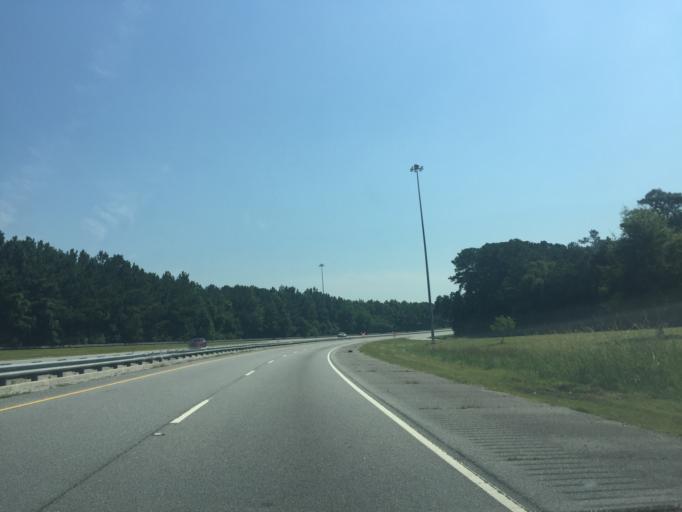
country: US
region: Georgia
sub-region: Chatham County
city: Garden City
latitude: 32.0403
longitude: -81.1633
